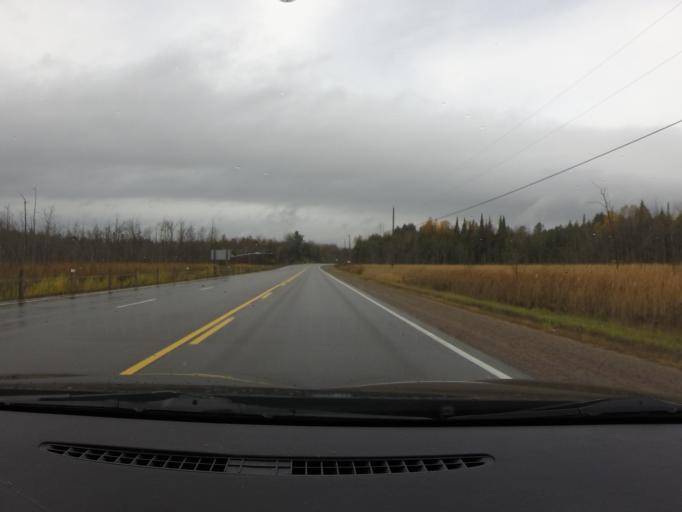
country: CA
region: Ontario
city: Belleville
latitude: 44.5572
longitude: -77.2893
